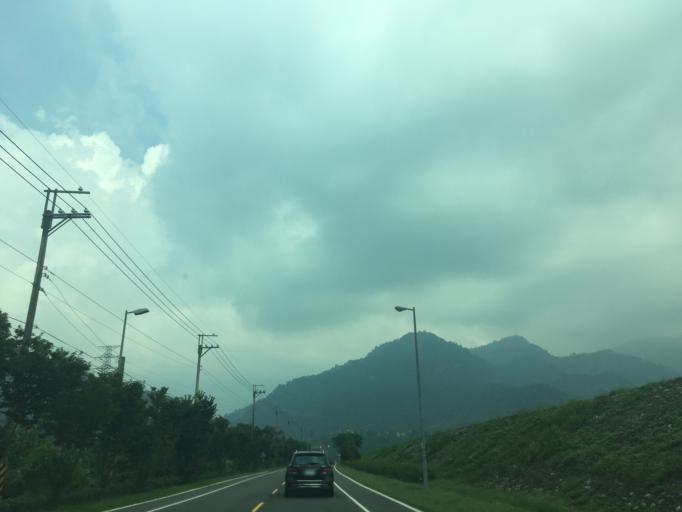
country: TW
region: Taiwan
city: Fengyuan
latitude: 24.2960
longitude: 120.8933
